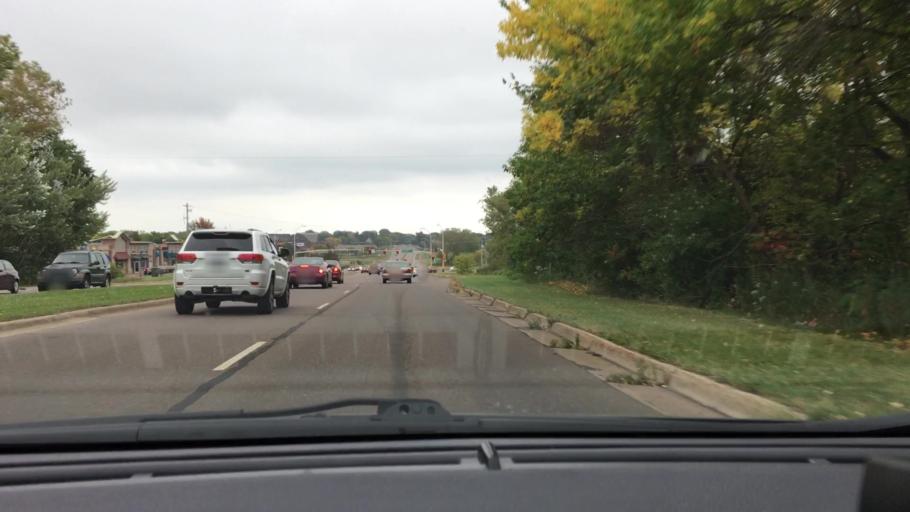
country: US
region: Minnesota
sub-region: Hennepin County
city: New Hope
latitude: 45.0331
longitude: -93.4115
